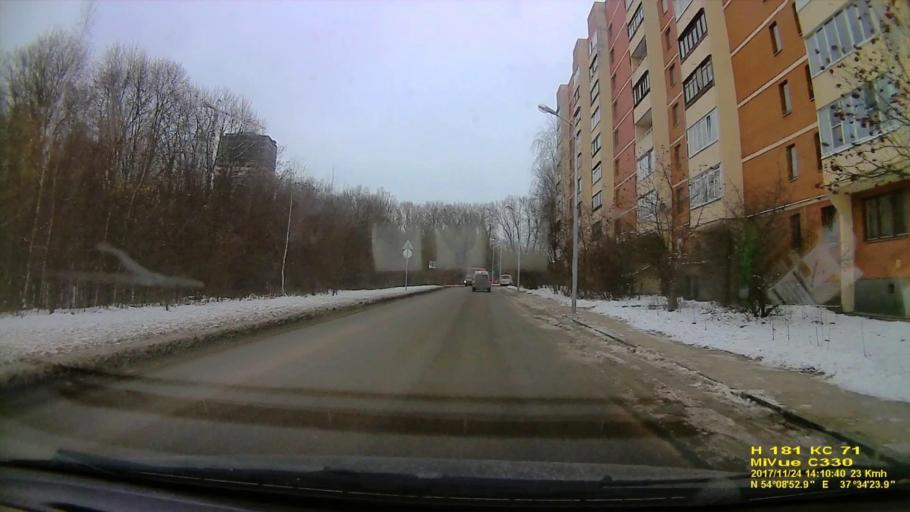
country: RU
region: Tula
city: Mendeleyevskiy
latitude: 54.1479
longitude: 37.5734
